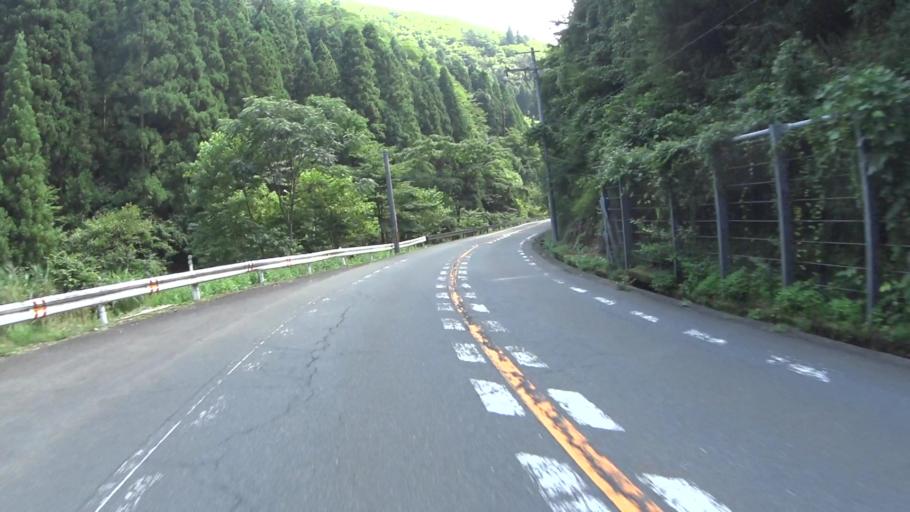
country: JP
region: Fukui
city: Obama
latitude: 35.3508
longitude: 135.5952
